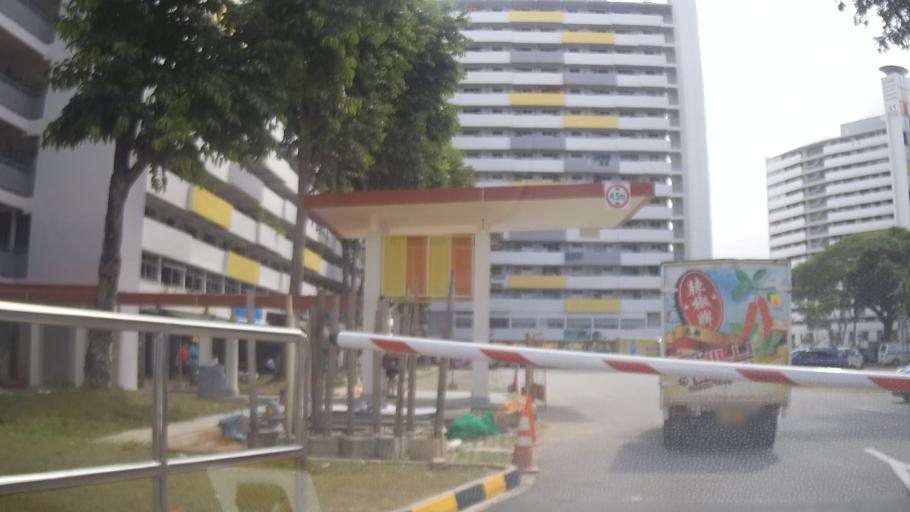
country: SG
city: Singapore
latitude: 1.3283
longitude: 103.8871
